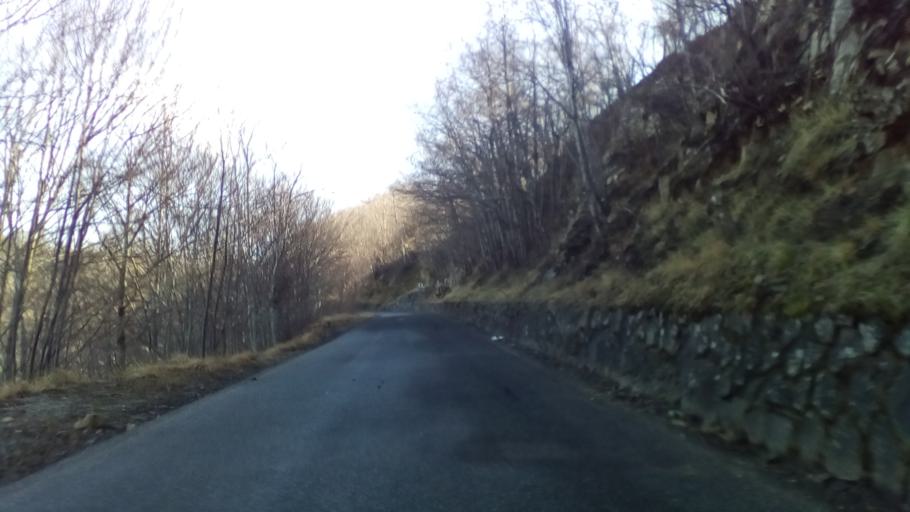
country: IT
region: Tuscany
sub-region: Provincia di Lucca
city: Castiglione di Garfagnana
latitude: 44.1651
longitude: 10.4477
